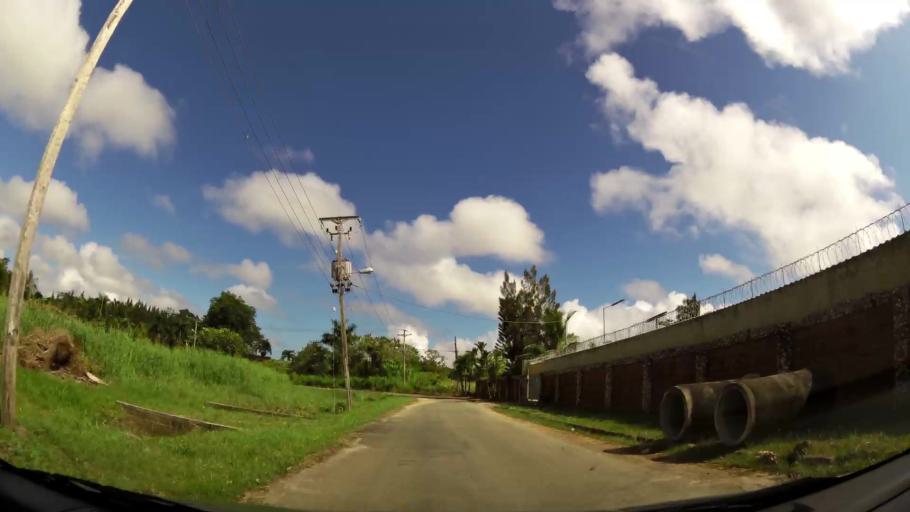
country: SR
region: Commewijne
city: Nieuw Amsterdam
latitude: 5.8727
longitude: -55.1012
